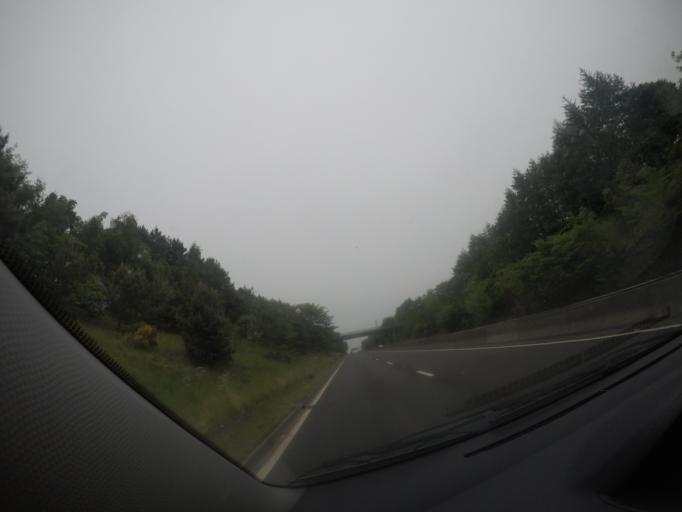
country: GB
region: Scotland
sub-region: Dundee City
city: Dundee
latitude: 56.5030
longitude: -2.9478
